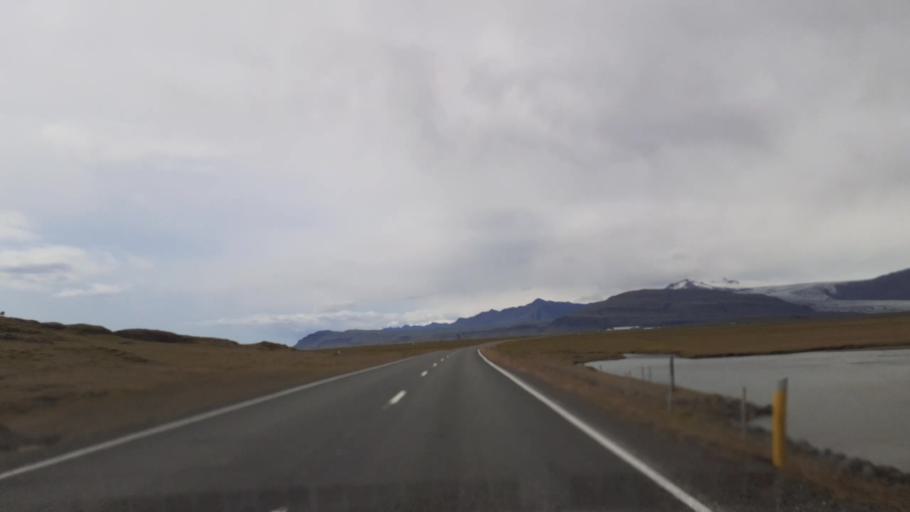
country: IS
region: East
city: Hoefn
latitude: 64.2656
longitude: -15.5148
